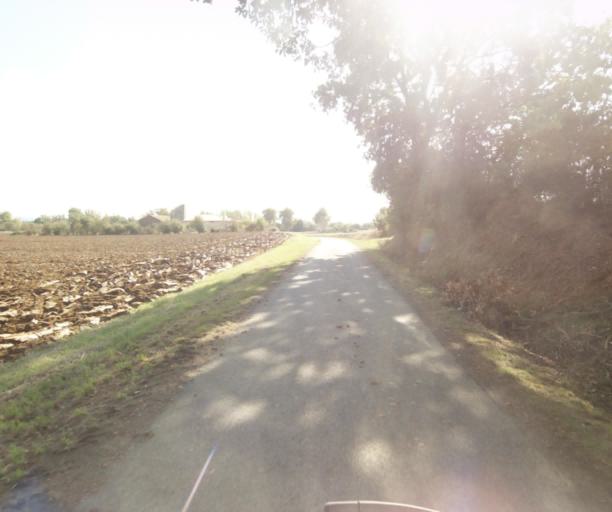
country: FR
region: Midi-Pyrenees
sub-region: Departement du Tarn-et-Garonne
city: Verdun-sur-Garonne
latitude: 43.8463
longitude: 1.1984
